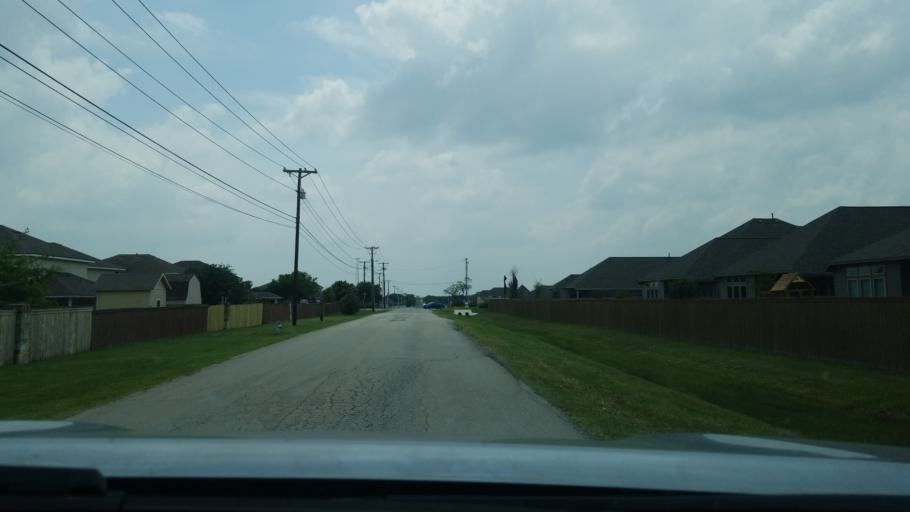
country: US
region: Texas
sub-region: Comal County
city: New Braunfels
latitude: 29.7530
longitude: -98.0695
